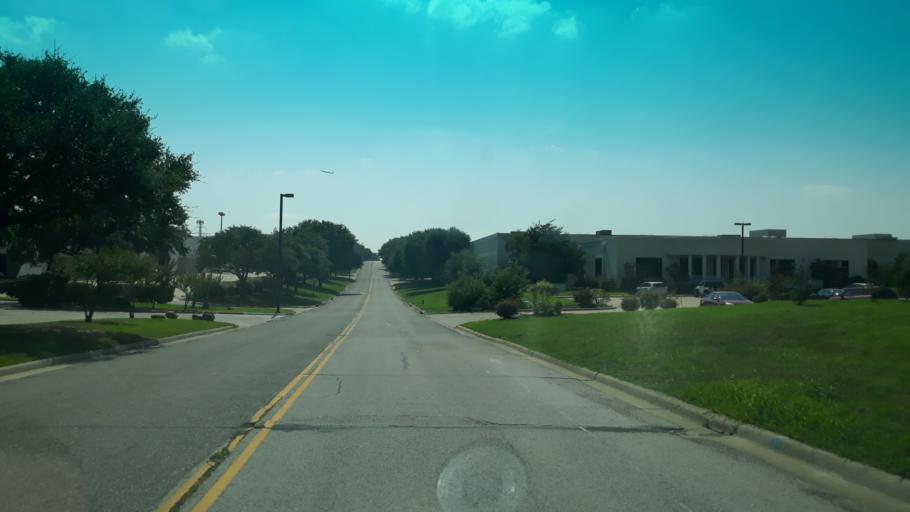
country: US
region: Texas
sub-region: Dallas County
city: Irving
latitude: 32.8697
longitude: -96.9845
